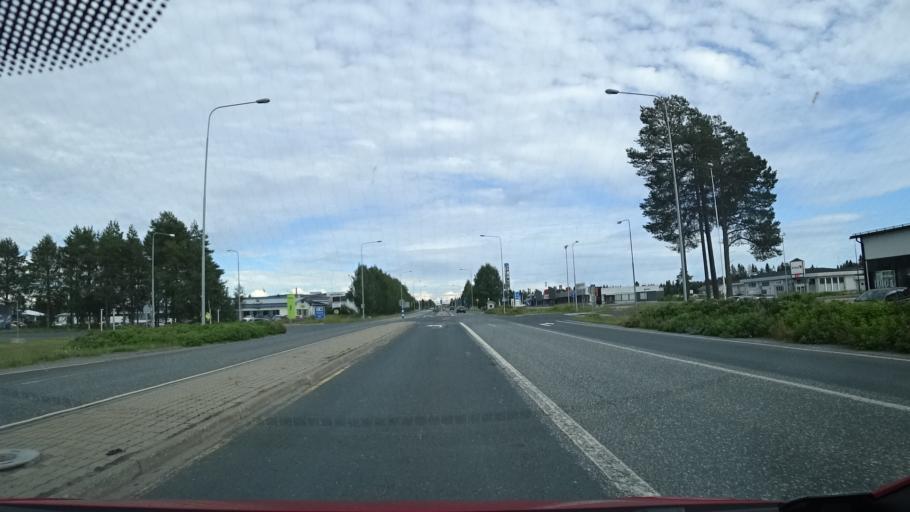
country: FI
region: Lapland
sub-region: Kemi-Tornio
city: Keminmaa
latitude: 65.7996
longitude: 24.5043
